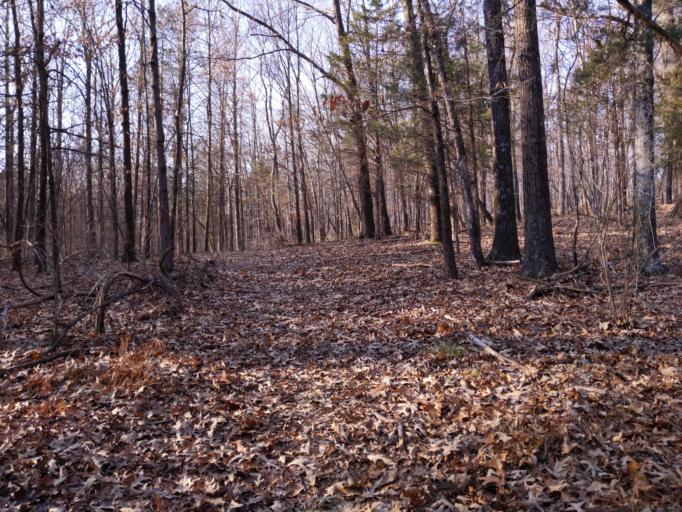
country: US
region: Virginia
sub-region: Loudoun County
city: Dulles Town Center
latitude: 39.0200
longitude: -77.4010
